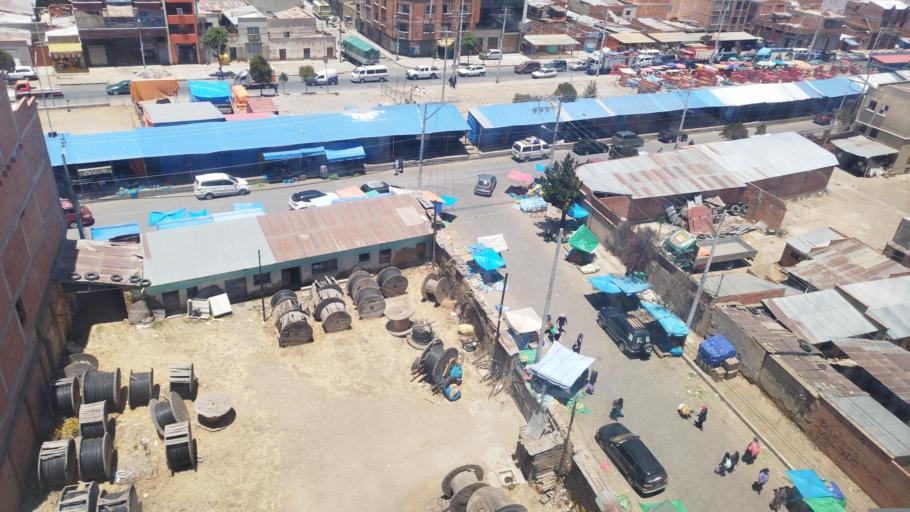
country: BO
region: La Paz
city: La Paz
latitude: -16.5090
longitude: -68.1563
